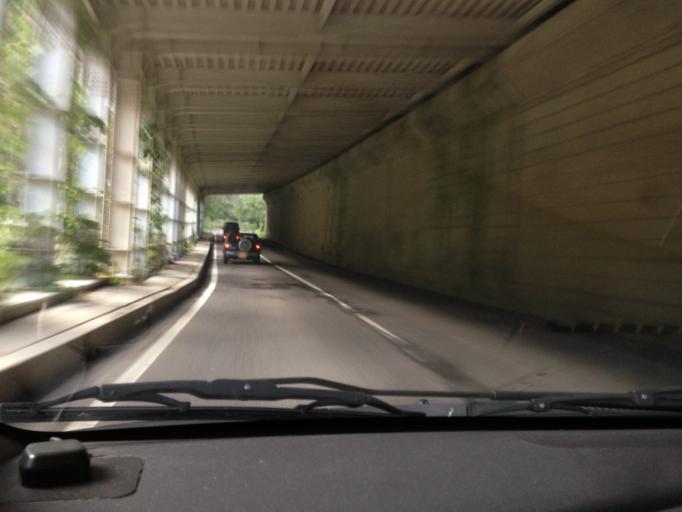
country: JP
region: Fukushima
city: Kitakata
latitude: 37.3929
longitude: 139.5486
